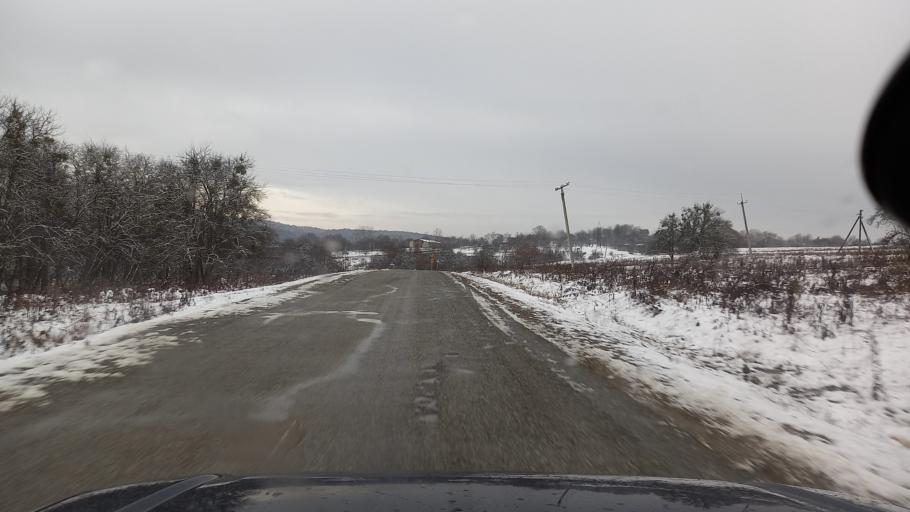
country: RU
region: Adygeya
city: Abadzekhskaya
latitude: 44.3593
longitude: 40.3991
